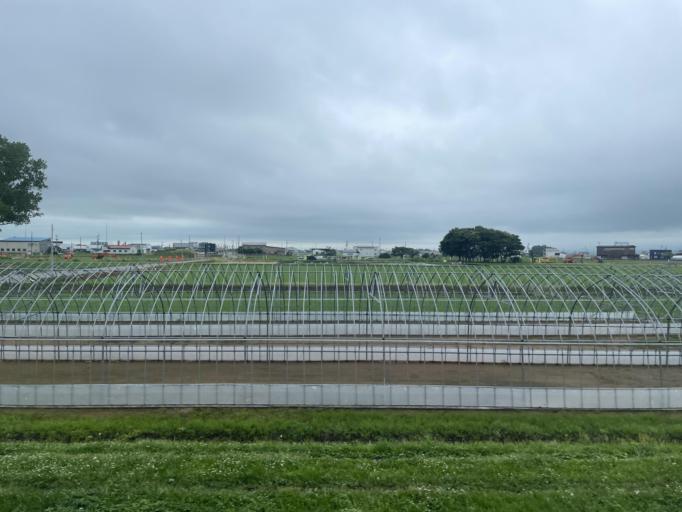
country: JP
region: Aomori
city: Shimokizukuri
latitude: 40.8067
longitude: 140.4049
